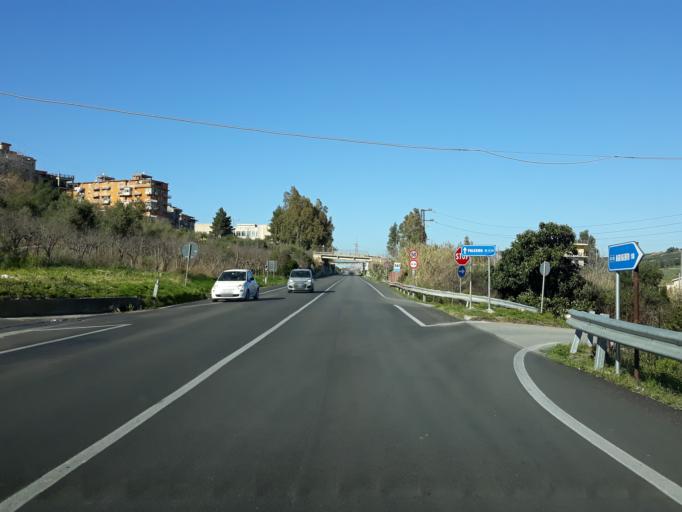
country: IT
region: Sicily
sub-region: Palermo
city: Misilmeri
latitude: 38.0345
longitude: 13.4586
